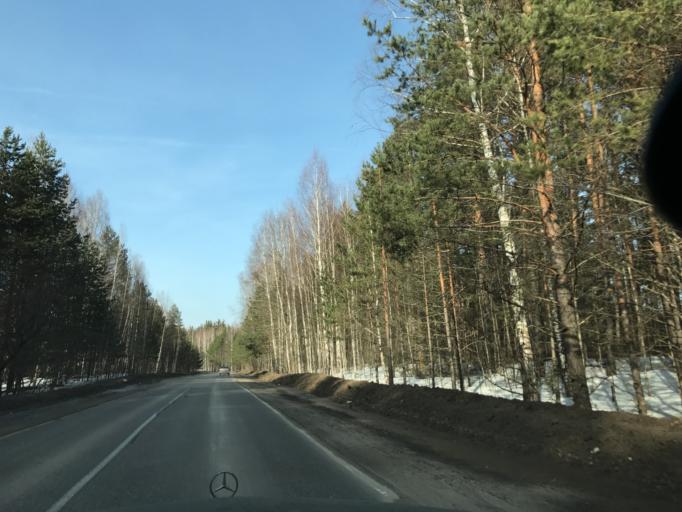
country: RU
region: Vladimir
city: Galitsy
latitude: 56.0048
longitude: 42.8600
